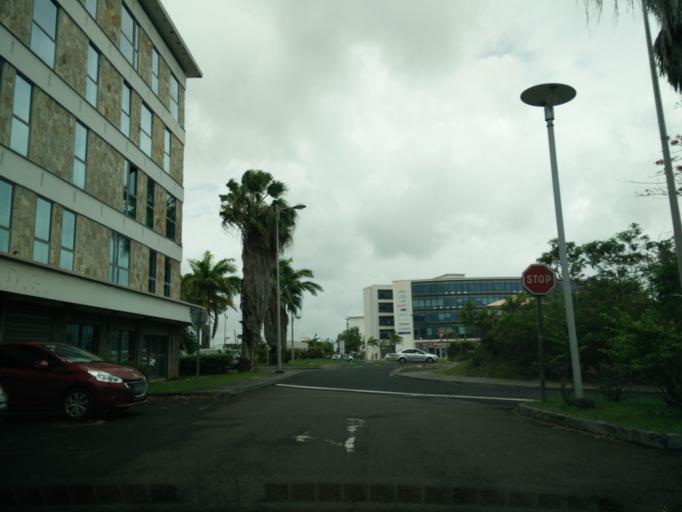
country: MQ
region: Martinique
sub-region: Martinique
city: Fort-de-France
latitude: 14.6034
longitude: -61.0428
